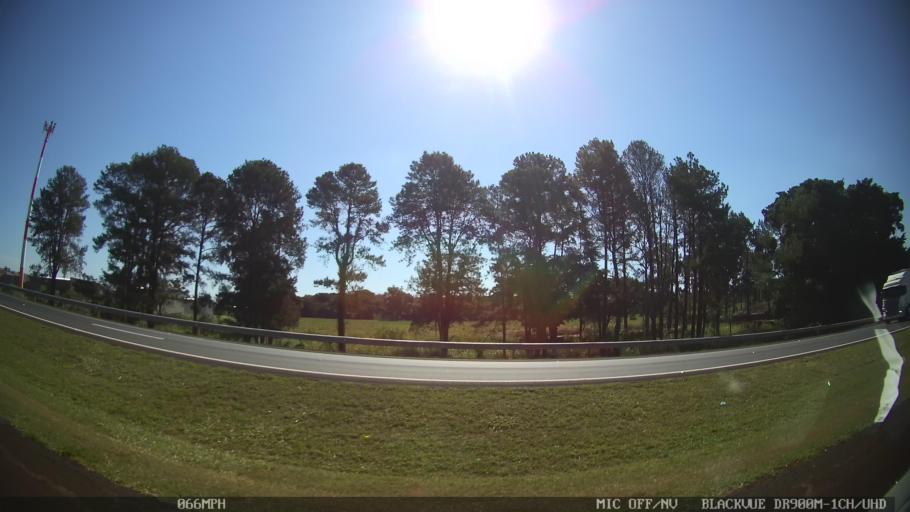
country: BR
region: Sao Paulo
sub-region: Ribeirao Preto
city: Ribeirao Preto
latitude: -21.1162
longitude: -47.8263
